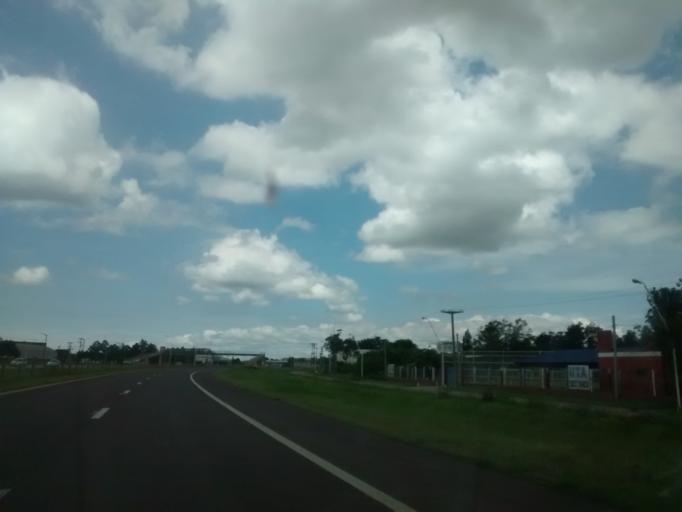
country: AR
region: Chaco
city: Fontana
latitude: -27.4087
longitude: -58.9865
